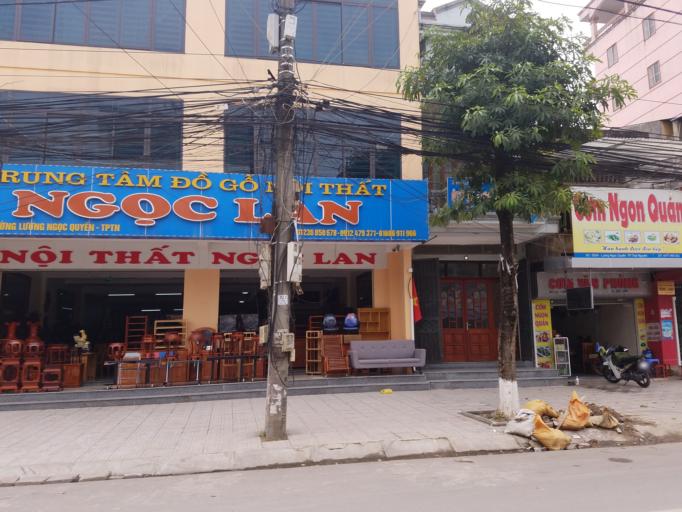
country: VN
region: Thai Nguyen
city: Thanh Pho Thai Nguyen
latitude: 21.5820
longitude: 105.8360
